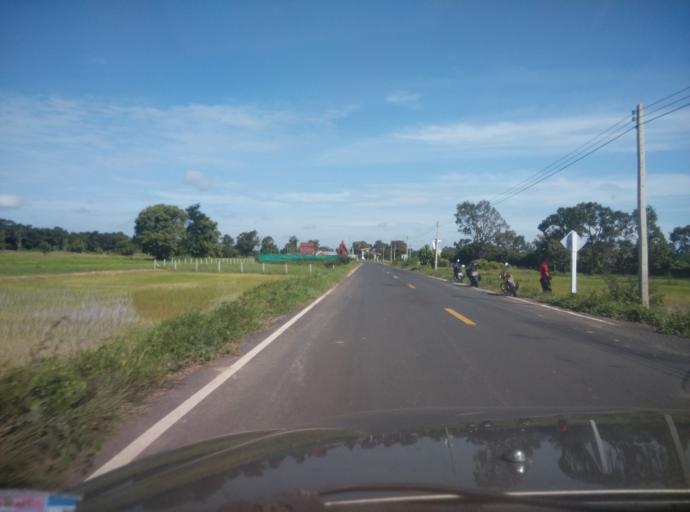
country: TH
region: Sisaket
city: Si Sa Ket
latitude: 15.1178
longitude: 104.2540
